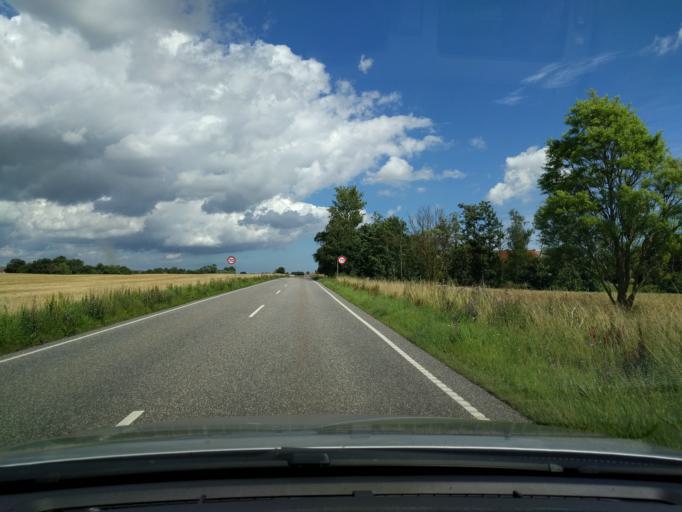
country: DK
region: Zealand
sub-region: Guldborgsund Kommune
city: Stubbekobing
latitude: 54.9104
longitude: 12.1329
